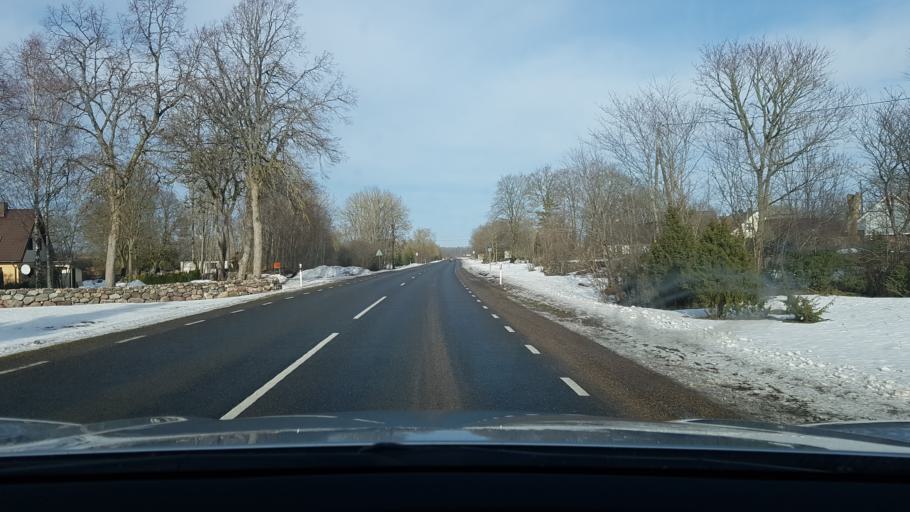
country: EE
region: Saare
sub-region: Kuressaare linn
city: Kuressaare
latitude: 58.2900
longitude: 22.5400
